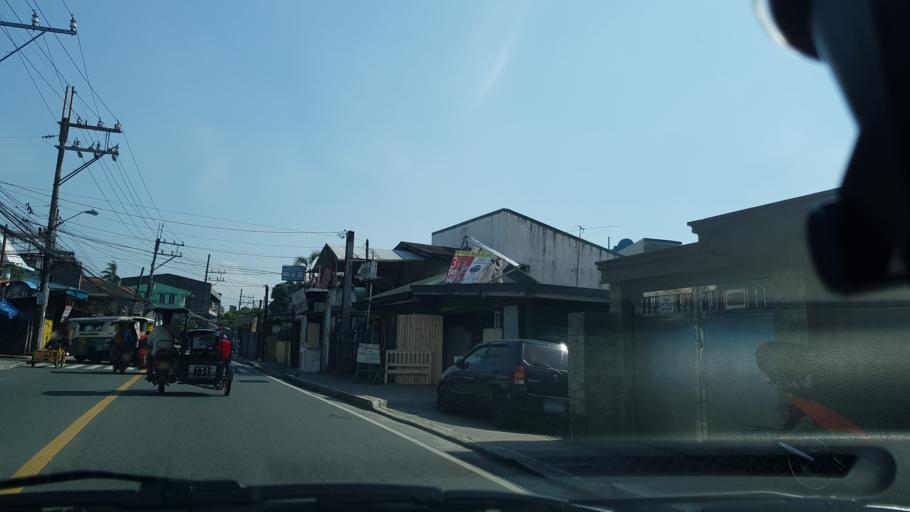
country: PH
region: Metro Manila
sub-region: Marikina
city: Calumpang
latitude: 14.6408
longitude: 121.0941
